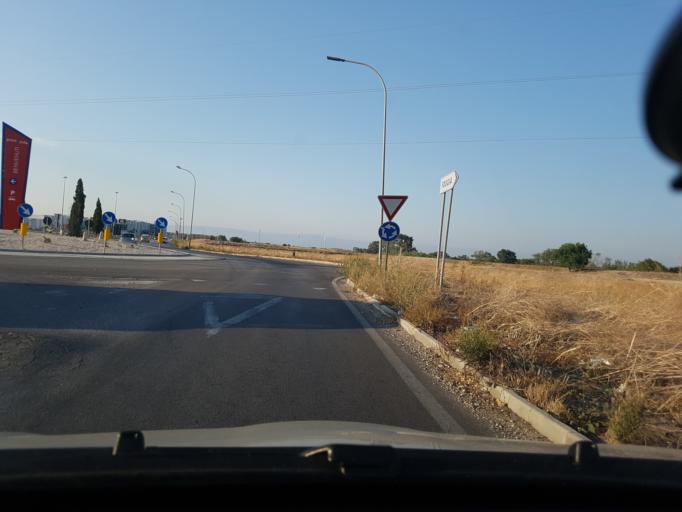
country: IT
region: Apulia
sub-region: Provincia di Foggia
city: Carapelle
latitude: 41.4107
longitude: 15.6535
